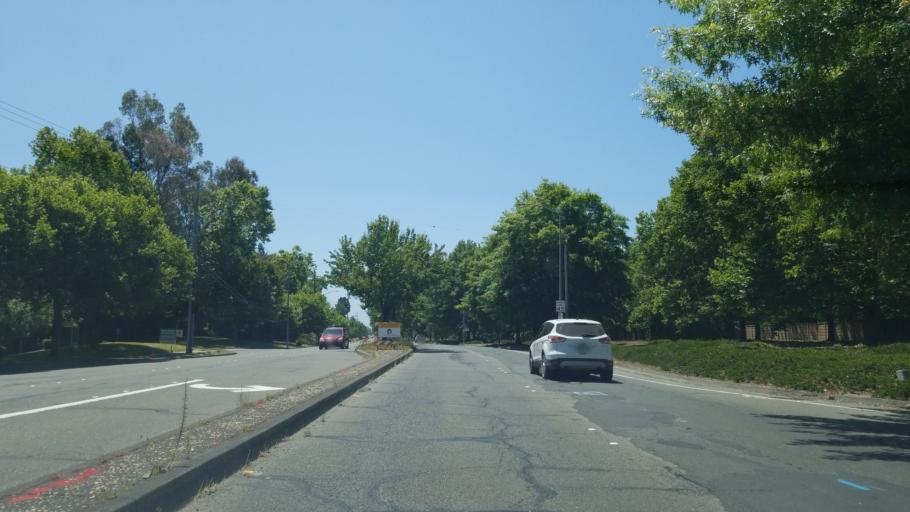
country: US
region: California
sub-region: Sonoma County
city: Roseland
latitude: 38.4376
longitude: -122.7704
